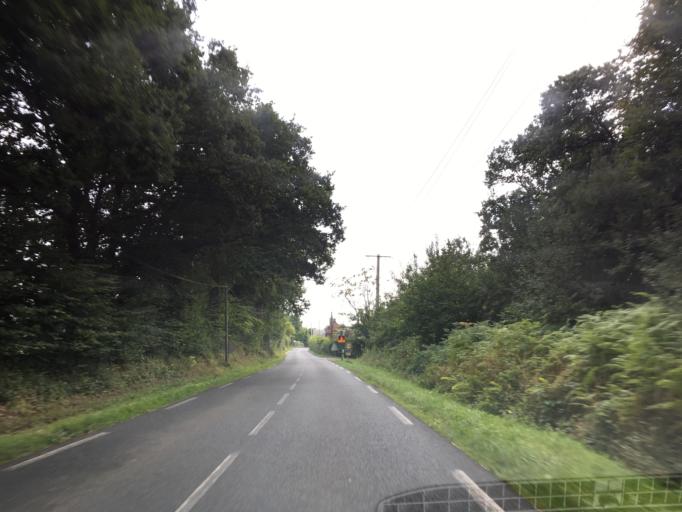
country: FR
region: Lower Normandy
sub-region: Departement du Calvados
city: Touques
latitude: 49.3404
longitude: 0.1358
